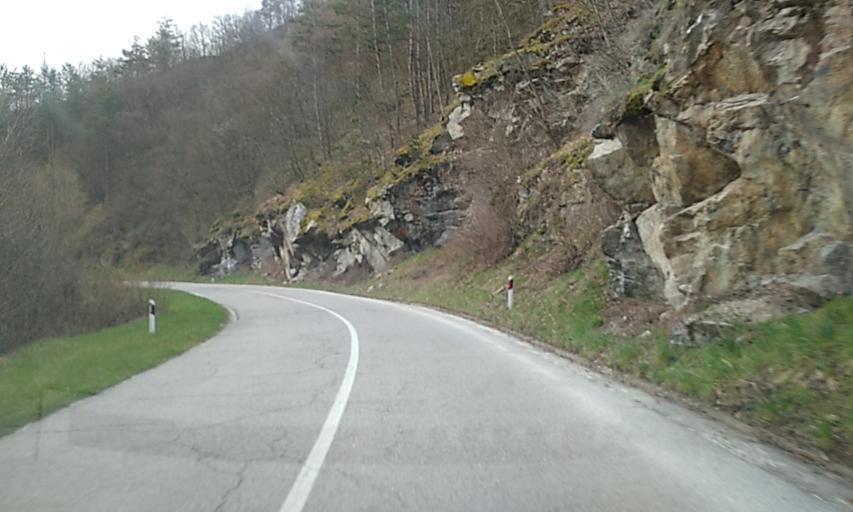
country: RS
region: Central Serbia
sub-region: Pcinjski Okrug
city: Bosilegrad
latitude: 42.5017
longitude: 22.4567
